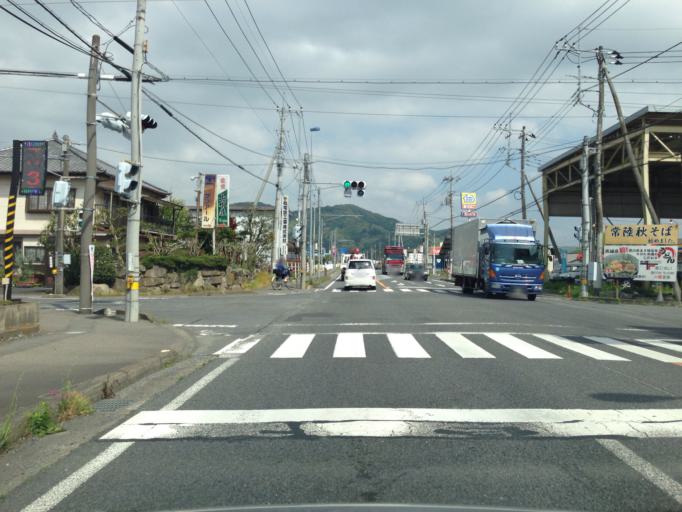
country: JP
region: Ibaraki
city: Iwase
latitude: 36.3580
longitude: 140.1434
